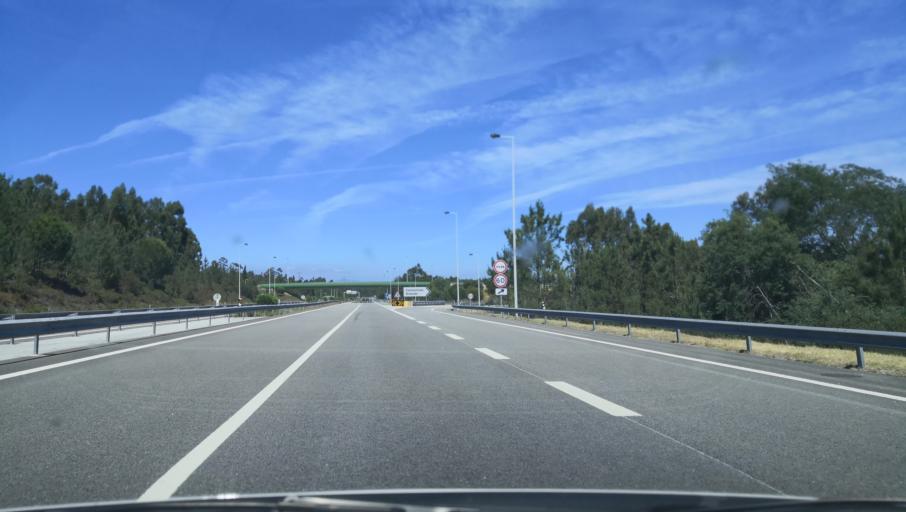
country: PT
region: Coimbra
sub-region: Montemor-O-Velho
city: Arazede
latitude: 40.2585
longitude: -8.6320
